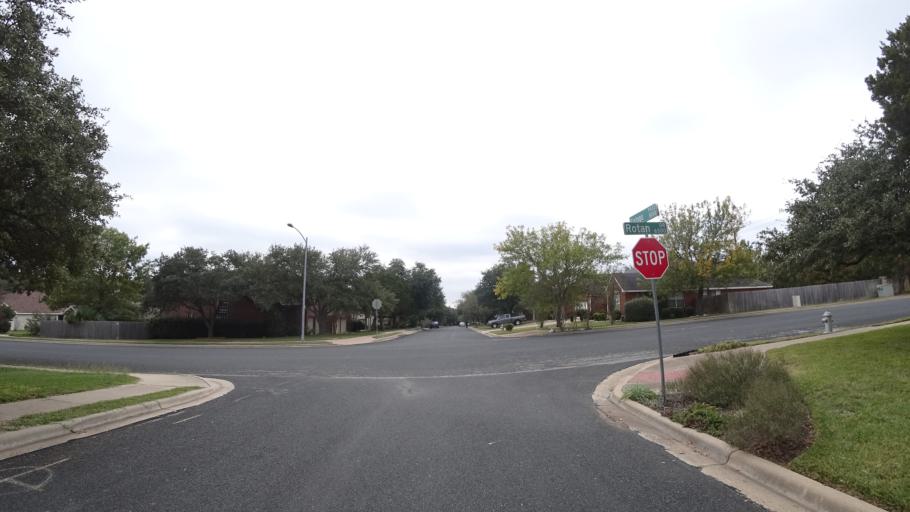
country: US
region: Texas
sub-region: Travis County
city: Shady Hollow
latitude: 30.2205
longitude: -97.8765
